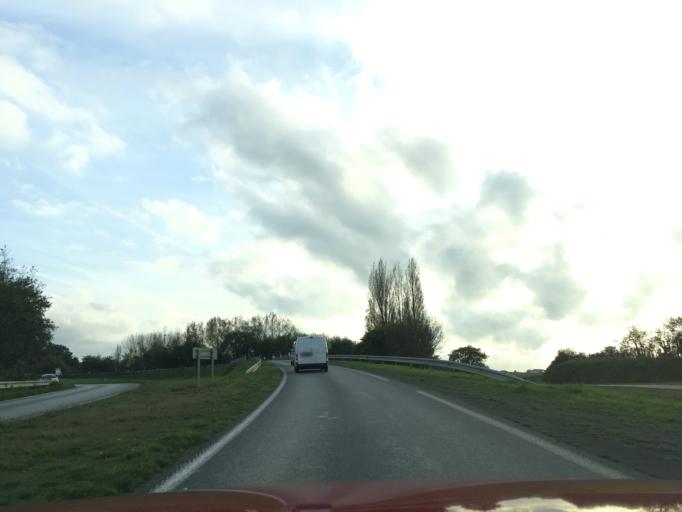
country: FR
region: Lower Normandy
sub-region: Departement de la Manche
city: Saint-Pair-sur-Mer
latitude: 48.8215
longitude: -1.5513
